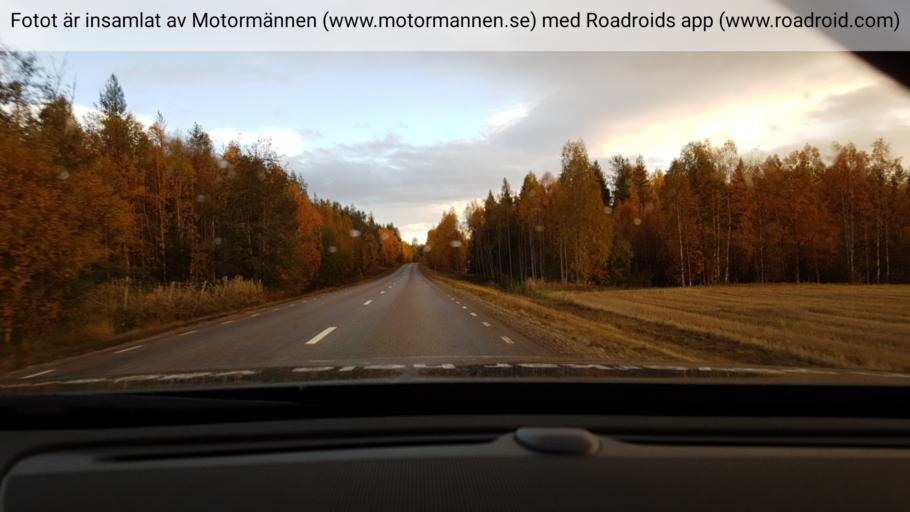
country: SE
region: Norrbotten
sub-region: Overkalix Kommun
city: OEverkalix
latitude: 66.4987
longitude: 22.7711
